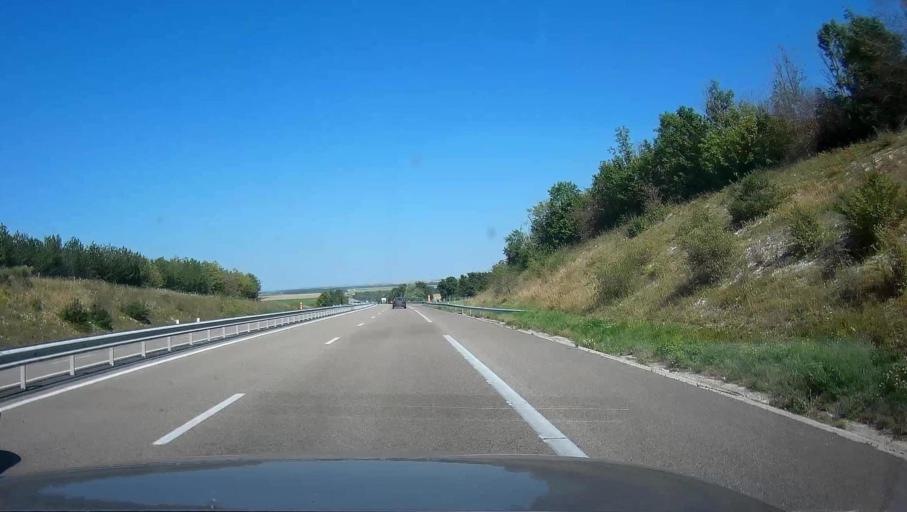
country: FR
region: Champagne-Ardenne
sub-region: Departement de l'Aube
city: Creney-pres-Troyes
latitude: 48.3776
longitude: 4.1573
